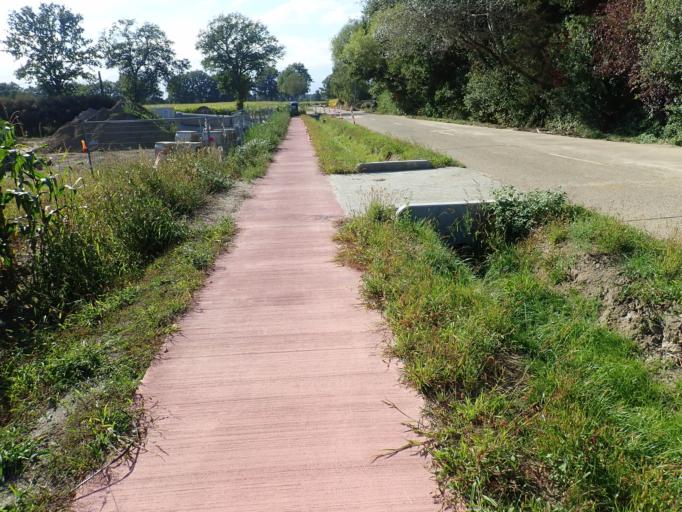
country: BE
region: Flanders
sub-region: Provincie Antwerpen
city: Nijlen
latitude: 51.1497
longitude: 4.7040
